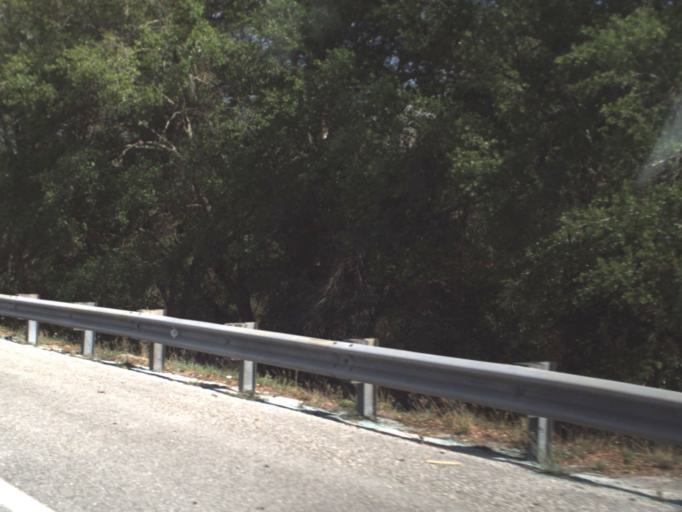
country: US
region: Florida
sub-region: Lake County
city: Lady Lake
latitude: 28.9292
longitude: -81.9267
